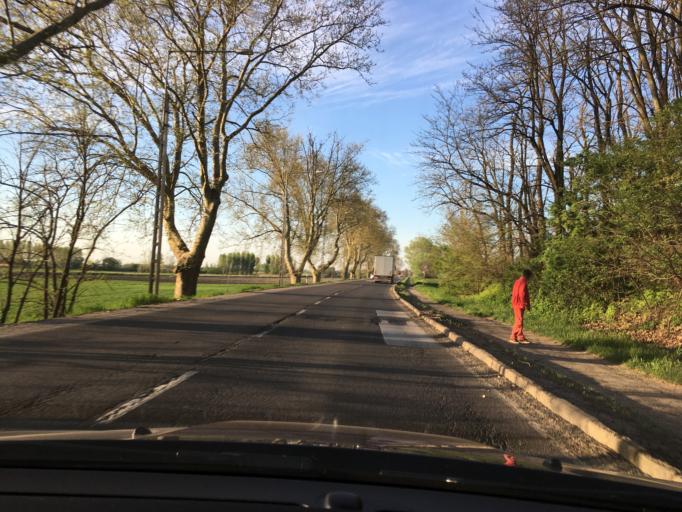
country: HU
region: Hajdu-Bihar
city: Mikepercs
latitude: 47.4312
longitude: 21.6268
